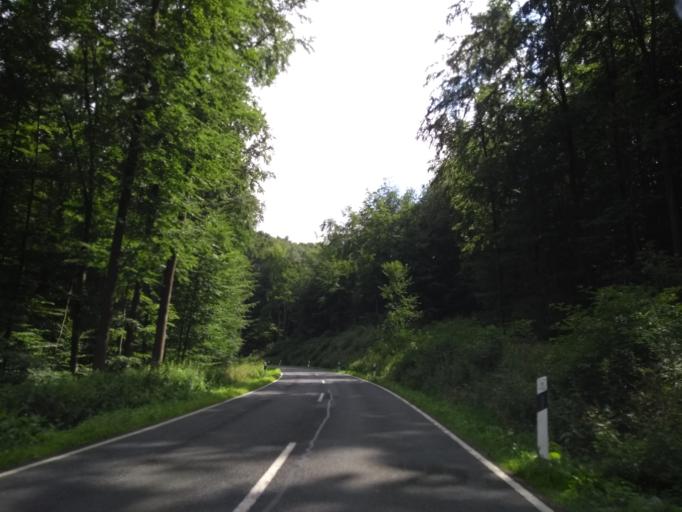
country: DE
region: Lower Saxony
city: Bad Pyrmont
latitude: 51.9667
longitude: 9.2976
